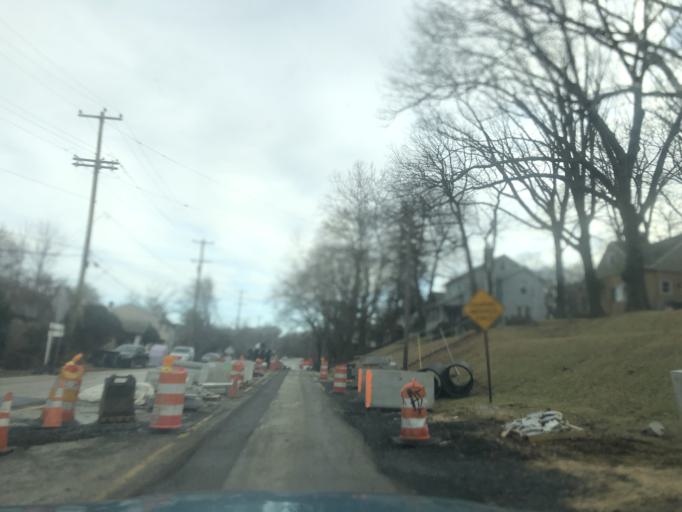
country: US
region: Pennsylvania
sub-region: Montgomery County
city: Glenside
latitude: 40.1191
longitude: -75.1374
